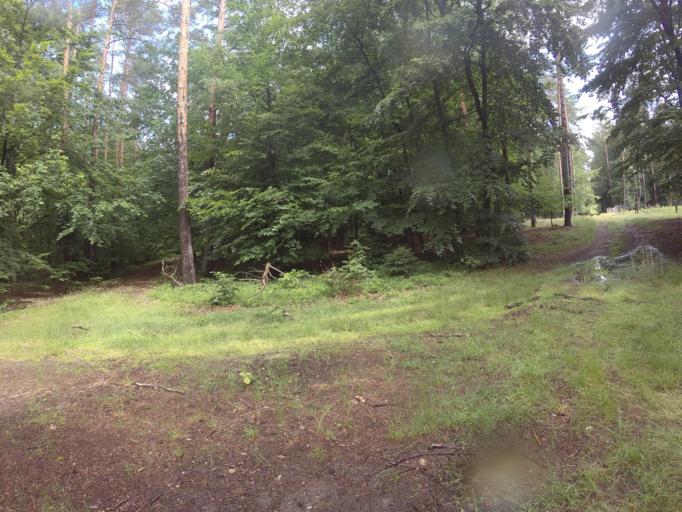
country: PL
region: West Pomeranian Voivodeship
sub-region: Powiat choszczenski
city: Bierzwnik
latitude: 53.0158
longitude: 15.5954
